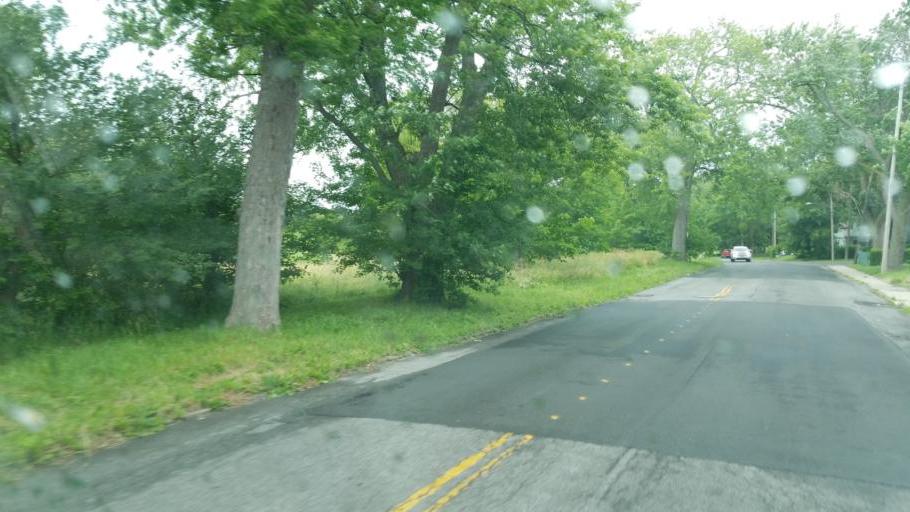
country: CA
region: Ontario
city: Niagara Falls
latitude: 43.1143
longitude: -79.0574
